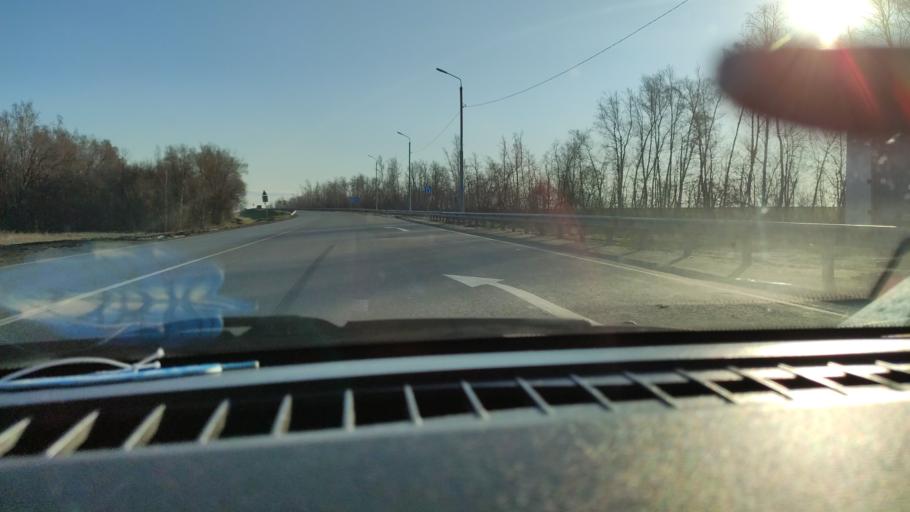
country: RU
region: Saratov
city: Balakovo
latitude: 52.0978
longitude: 47.7305
